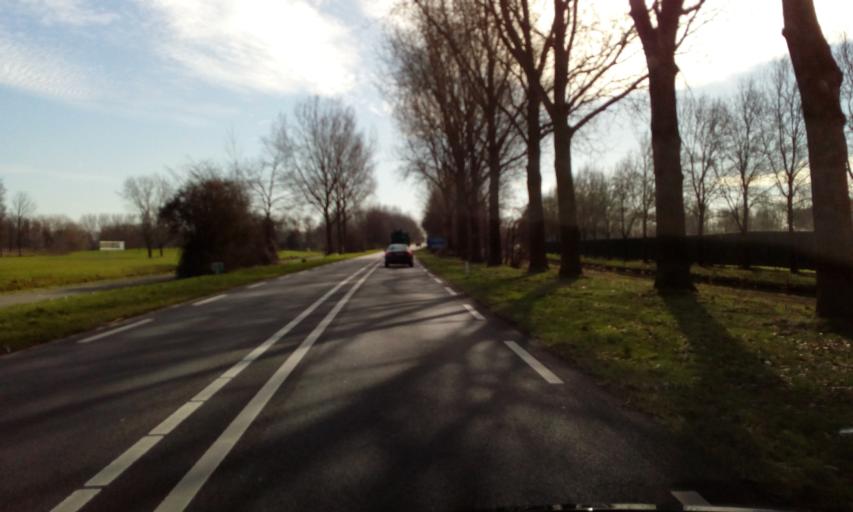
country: NL
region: South Holland
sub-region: Gemeente Alphen aan den Rijn
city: Alphen aan den Rijn
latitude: 52.1465
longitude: 4.6972
